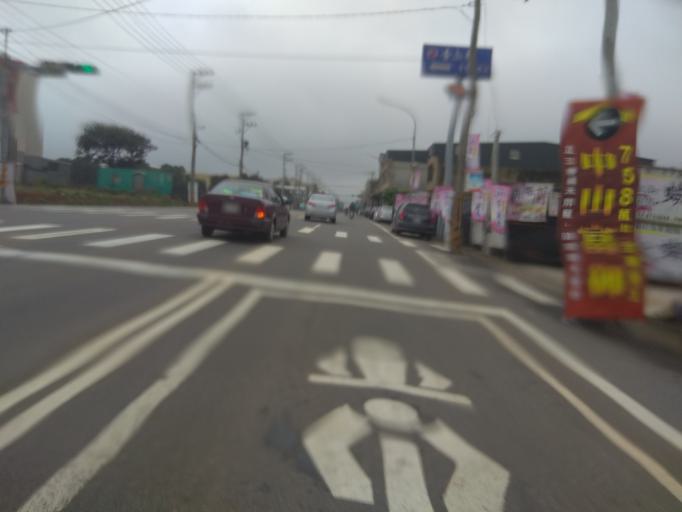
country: TW
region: Taiwan
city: Taoyuan City
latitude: 25.0289
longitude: 121.1072
